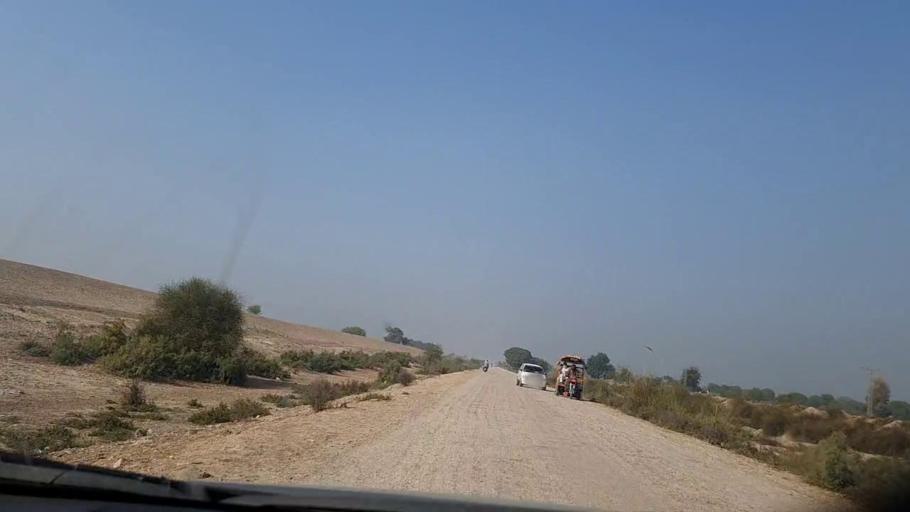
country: PK
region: Sindh
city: Moro
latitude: 26.7131
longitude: 67.9244
